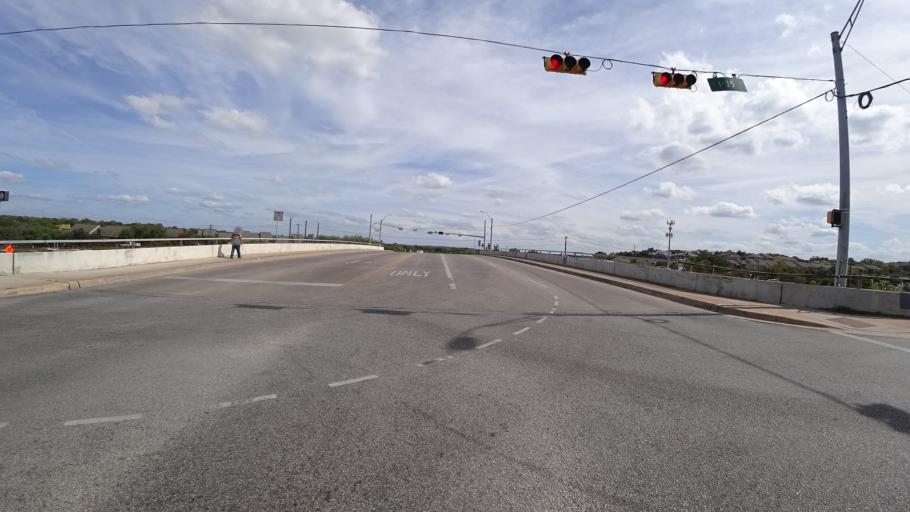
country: US
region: Texas
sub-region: Travis County
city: Onion Creek
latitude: 30.1986
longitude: -97.7644
